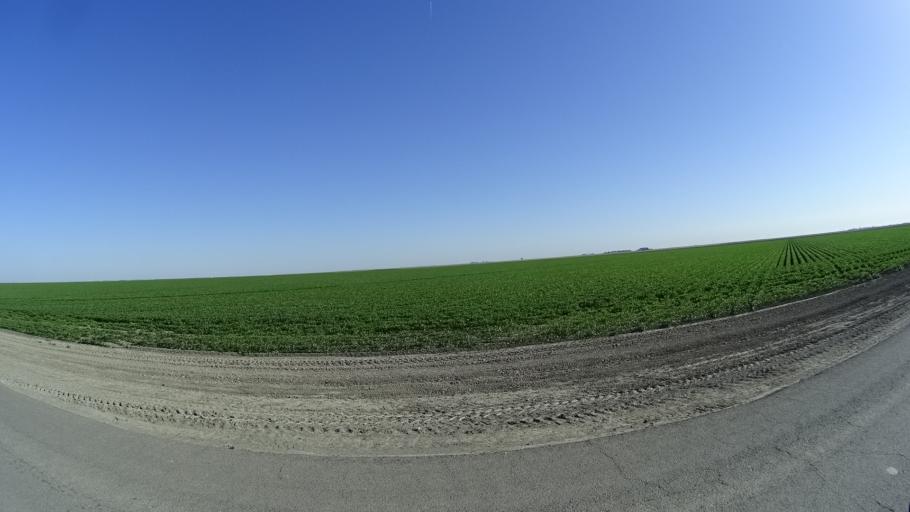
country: US
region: California
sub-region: Kings County
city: Corcoran
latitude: 36.0797
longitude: -119.6521
